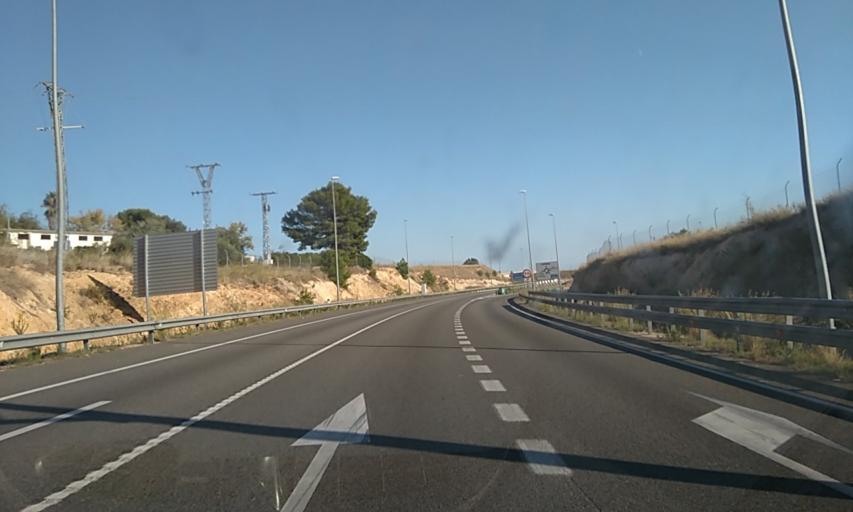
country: ES
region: Valencia
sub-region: Provincia de Castello
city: Torreblanca
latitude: 40.2303
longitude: 0.2109
